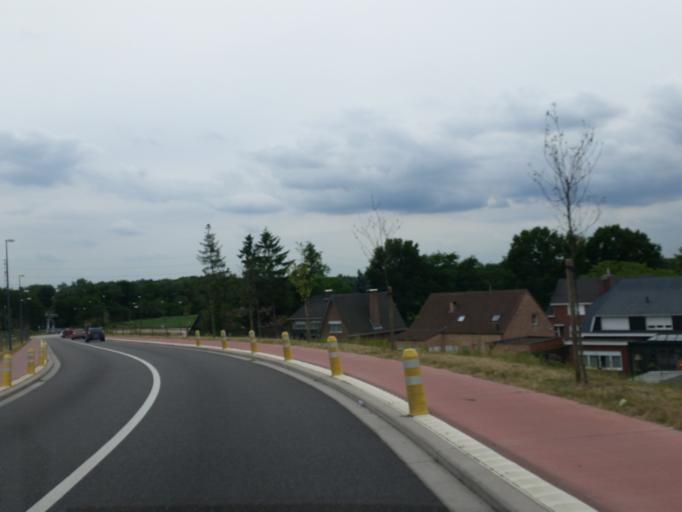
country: BE
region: Flanders
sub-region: Provincie Antwerpen
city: Ranst
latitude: 51.2060
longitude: 4.5990
